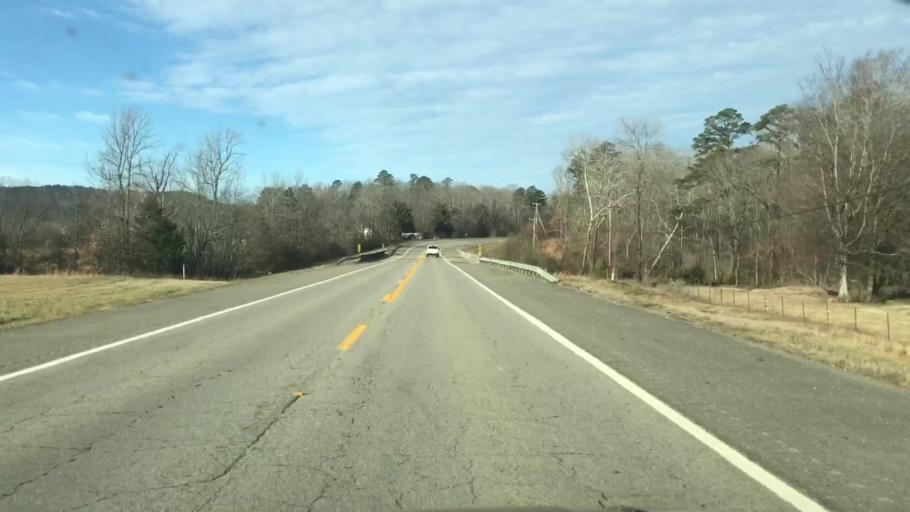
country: US
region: Arkansas
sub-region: Montgomery County
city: Mount Ida
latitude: 34.5396
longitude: -93.5997
